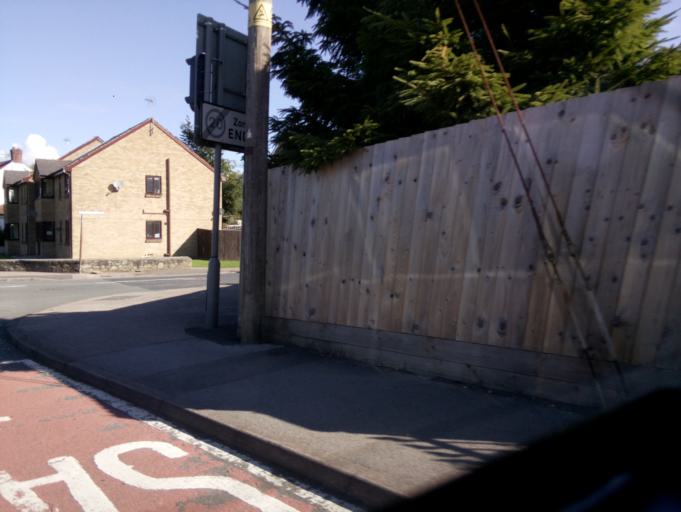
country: GB
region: England
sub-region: Gloucestershire
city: Coleford
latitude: 51.7909
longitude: -2.6027
